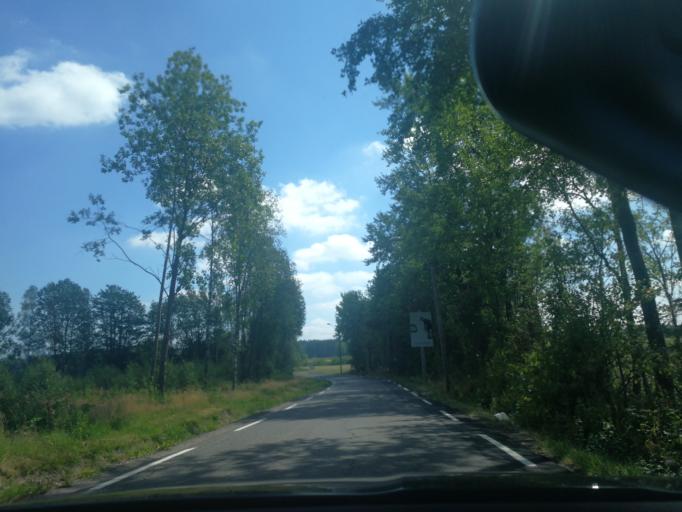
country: NO
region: Vestfold
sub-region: Stokke
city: Stokke
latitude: 59.2066
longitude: 10.2457
